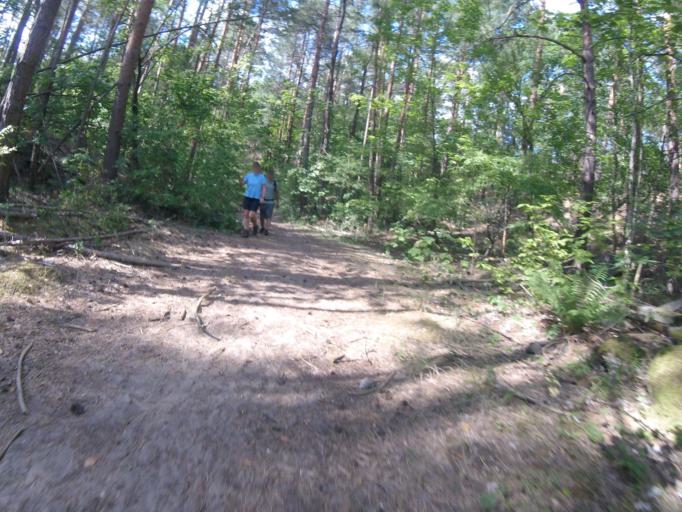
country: DE
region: Brandenburg
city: Wildau
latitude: 52.3310
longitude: 13.6675
